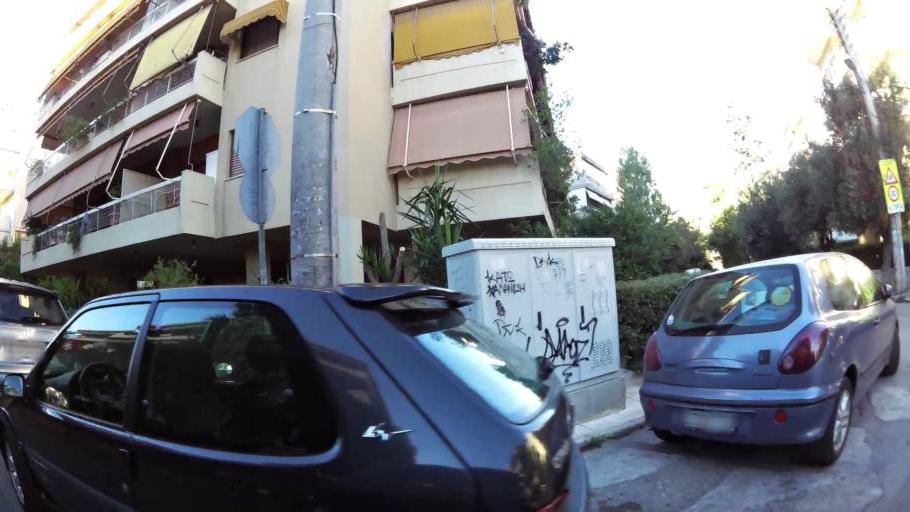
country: GR
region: Attica
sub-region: Nomarchia Athinas
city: Cholargos
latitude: 38.0096
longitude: 23.7988
